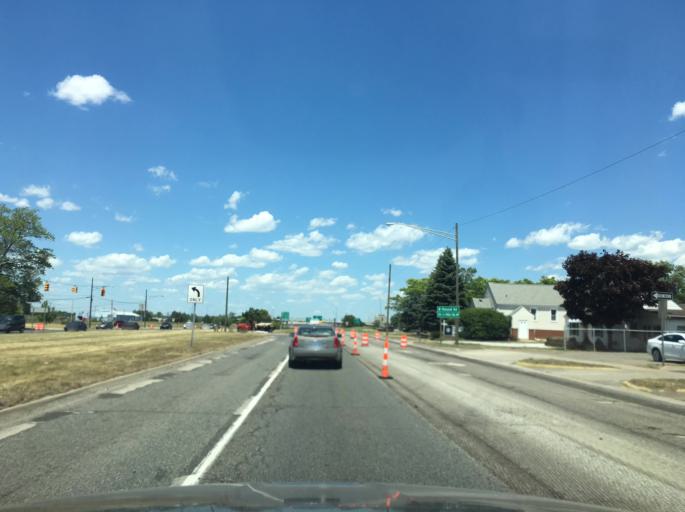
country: US
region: Michigan
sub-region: Macomb County
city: Warren
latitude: 42.4780
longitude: -83.0453
